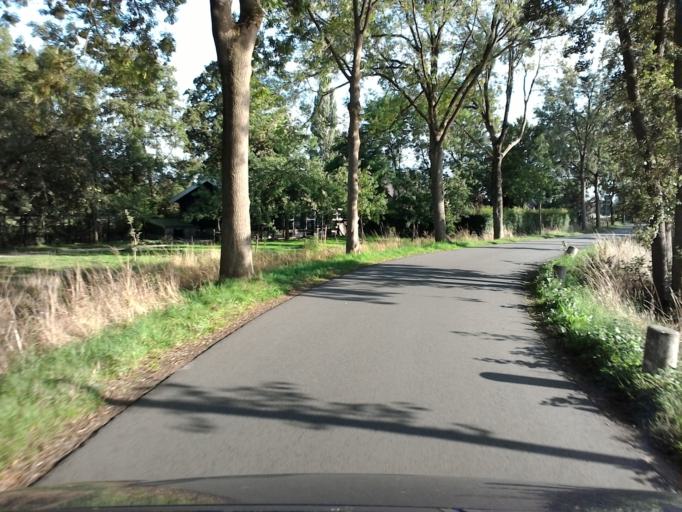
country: NL
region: Utrecht
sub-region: Gemeente De Bilt
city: De Bilt
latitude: 52.1100
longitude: 5.1609
